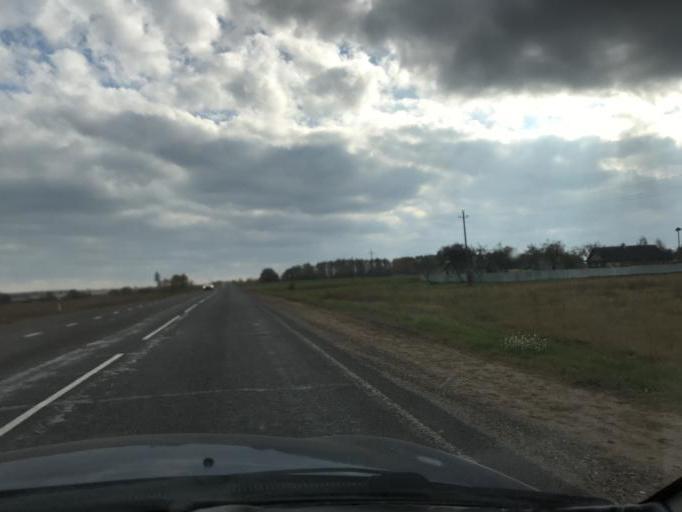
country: BY
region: Grodnenskaya
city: Lida
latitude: 53.7856
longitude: 25.1577
